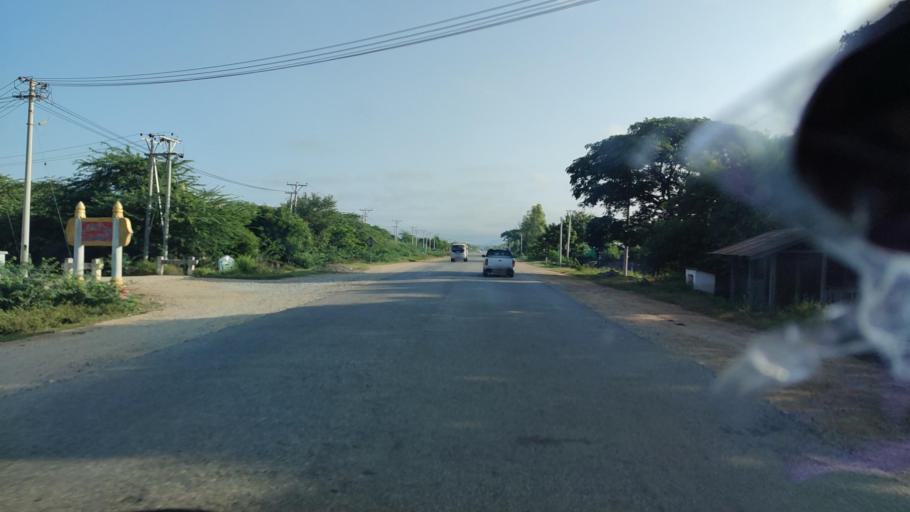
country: MM
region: Mandalay
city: Yamethin
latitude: 20.6734
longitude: 96.1391
